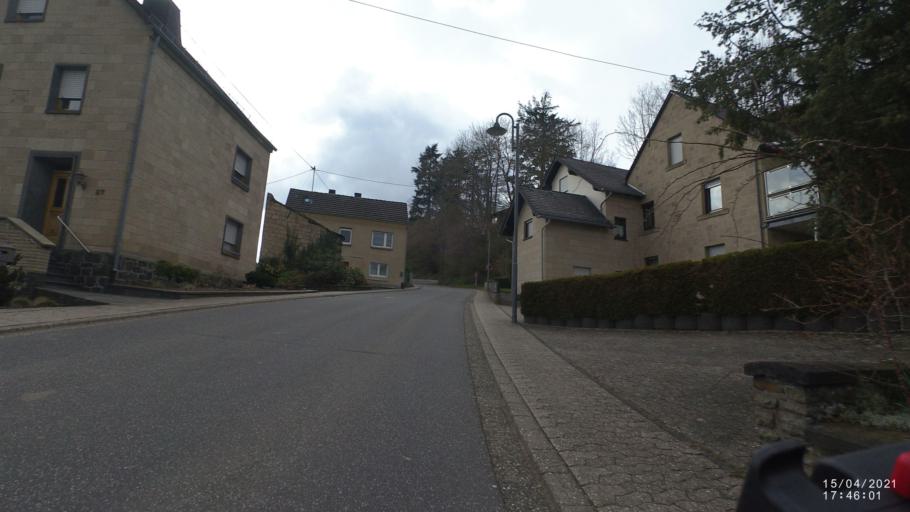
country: DE
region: Rheinland-Pfalz
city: Volkesfeld
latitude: 50.3909
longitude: 7.1471
